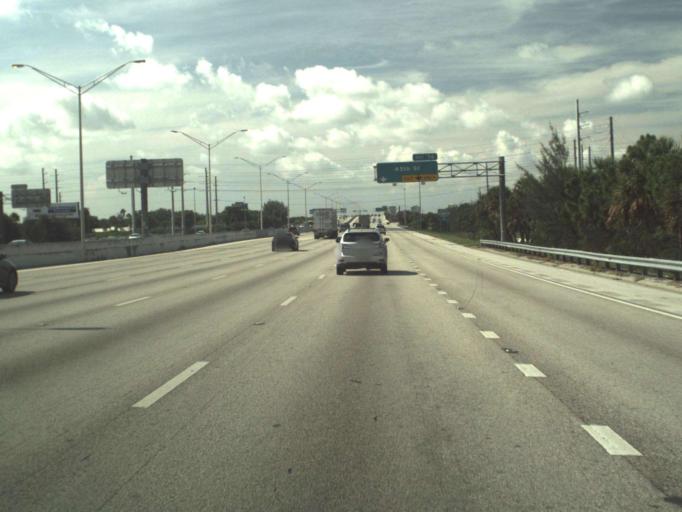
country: US
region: Florida
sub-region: Palm Beach County
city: Mangonia Park
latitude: 26.7681
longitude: -80.0950
